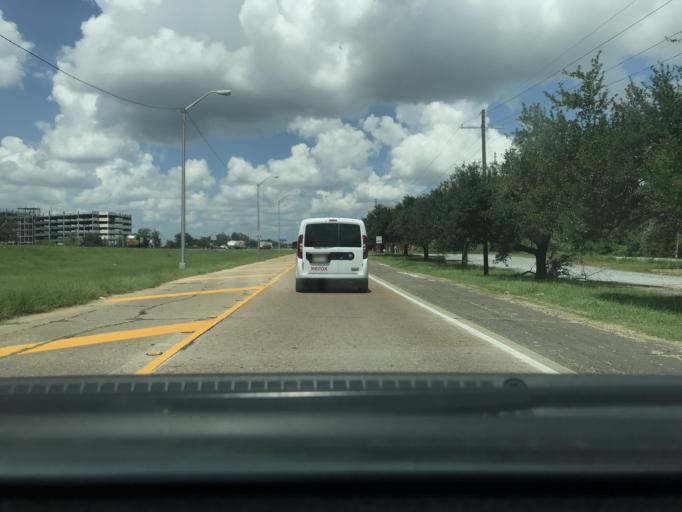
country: US
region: Louisiana
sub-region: Calcasieu Parish
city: Westlake
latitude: 30.2373
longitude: -93.2222
